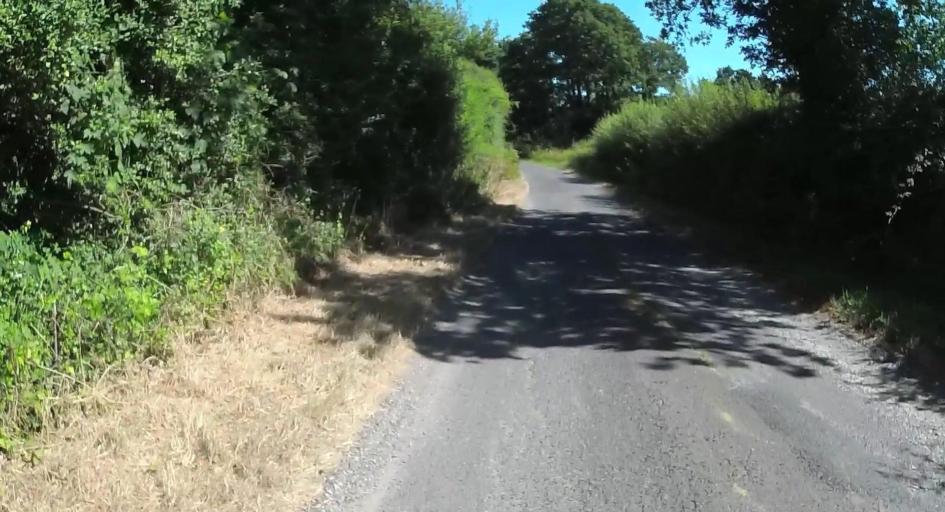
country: GB
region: England
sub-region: Dorset
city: Bovington Camp
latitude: 50.7277
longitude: -2.2018
